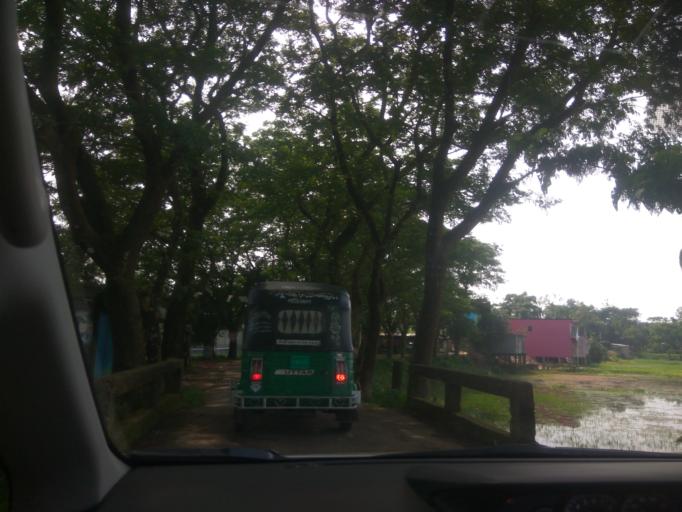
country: IN
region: Assam
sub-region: Karimganj
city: Karimganj
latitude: 24.8091
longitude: 92.1840
